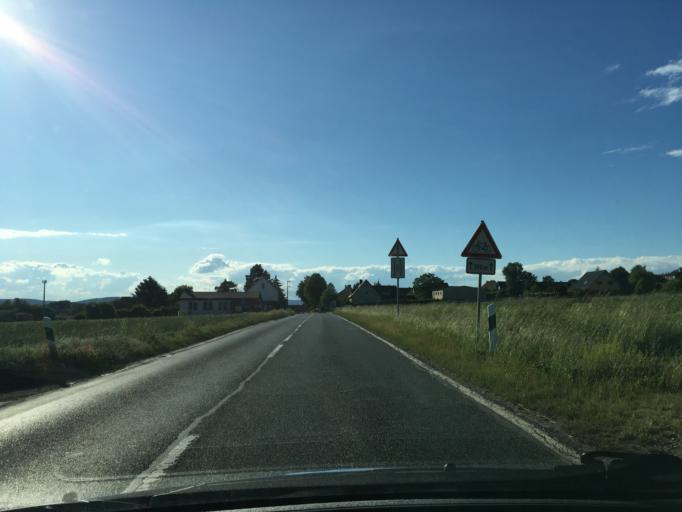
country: DE
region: Lower Saxony
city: Duingen
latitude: 52.0014
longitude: 9.7082
